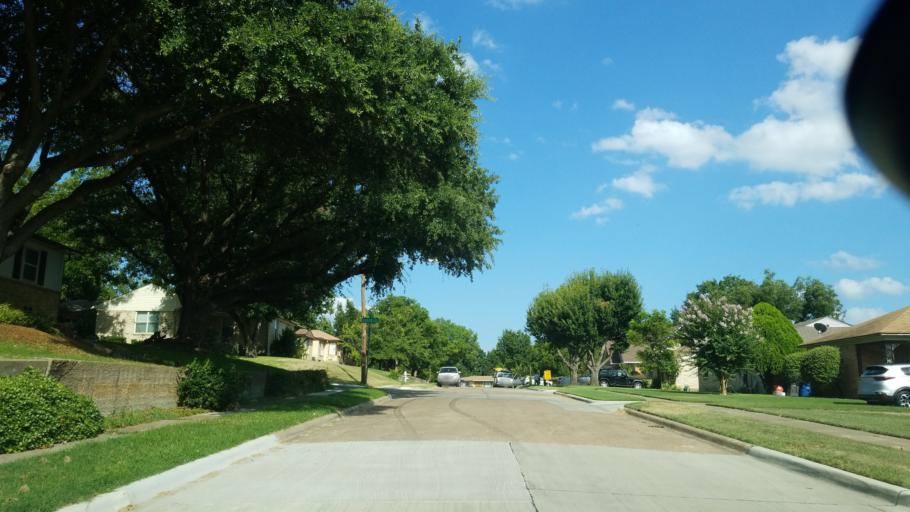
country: US
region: Texas
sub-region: Dallas County
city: Dallas
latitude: 32.7688
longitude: -96.7156
